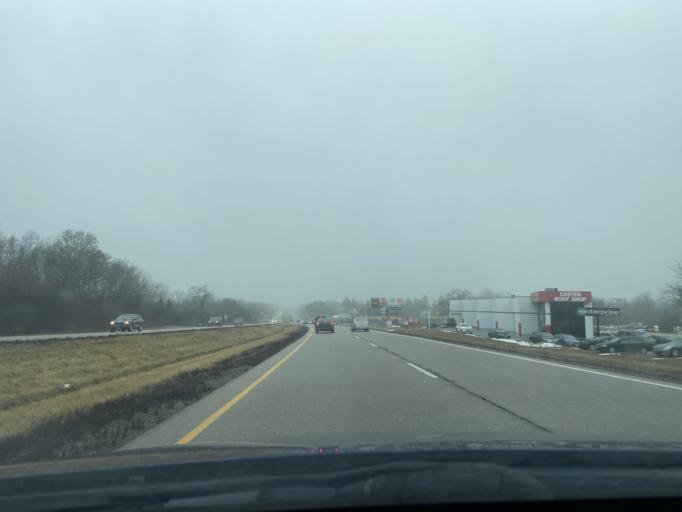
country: US
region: Illinois
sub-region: Lake County
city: Wauconda
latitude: 42.2451
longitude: -88.1236
